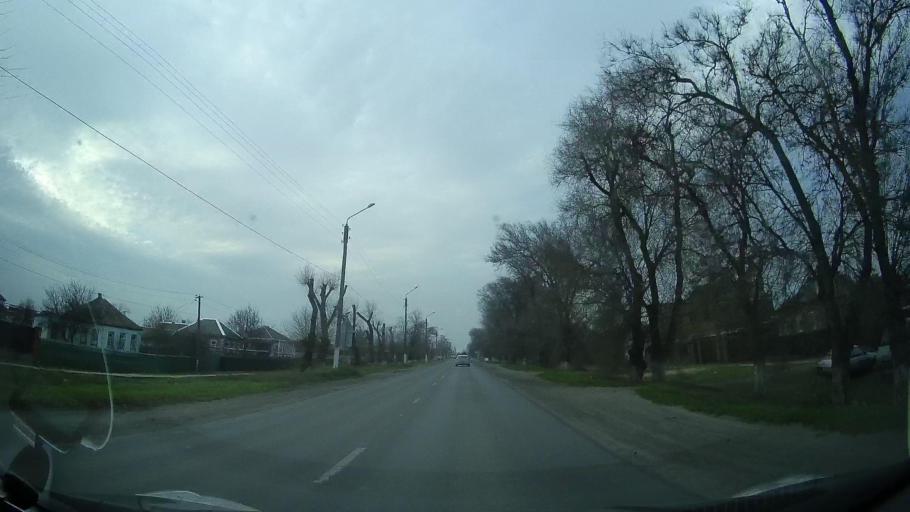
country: RU
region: Rostov
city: Ol'ginskaya
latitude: 47.1941
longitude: 39.9426
